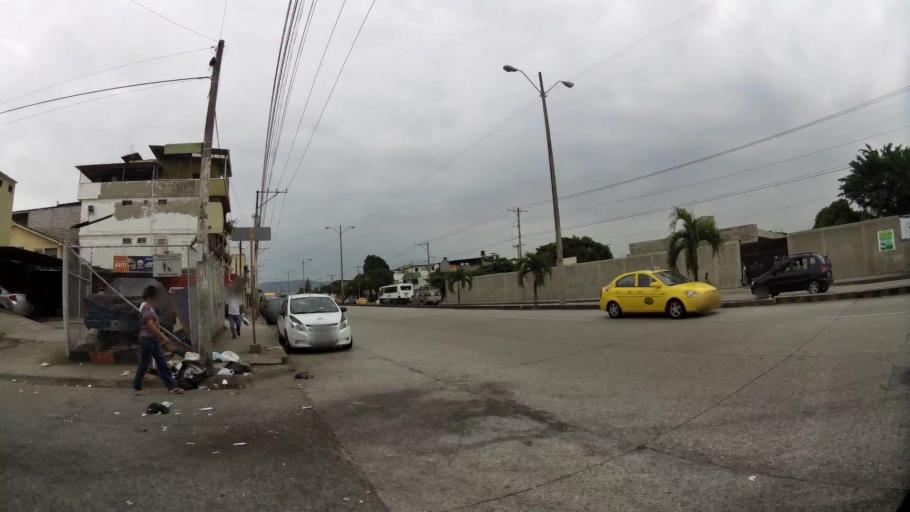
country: EC
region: Guayas
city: Eloy Alfaro
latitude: -2.1401
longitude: -79.8856
